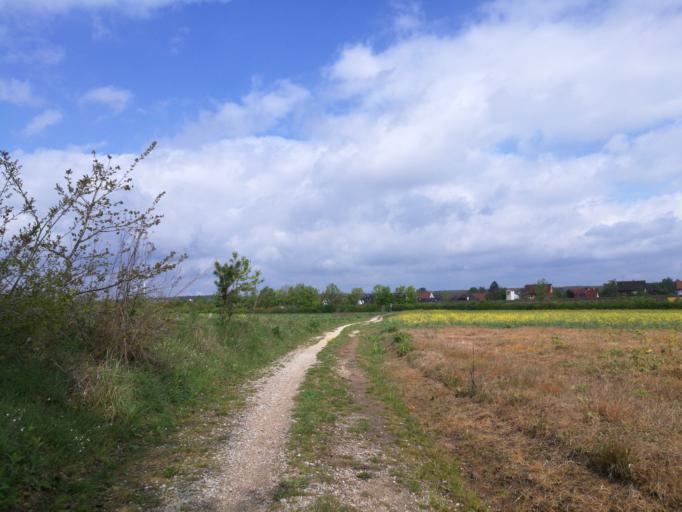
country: DE
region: Bavaria
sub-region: Regierungsbezirk Mittelfranken
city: Seukendorf
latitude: 49.4775
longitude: 10.8983
